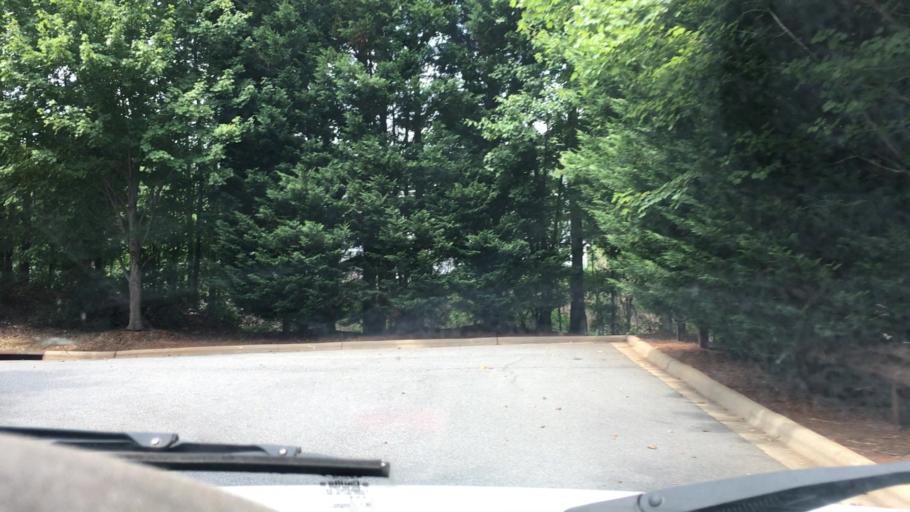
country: US
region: North Carolina
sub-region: Mecklenburg County
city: Cornelius
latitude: 35.4747
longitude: -80.8951
